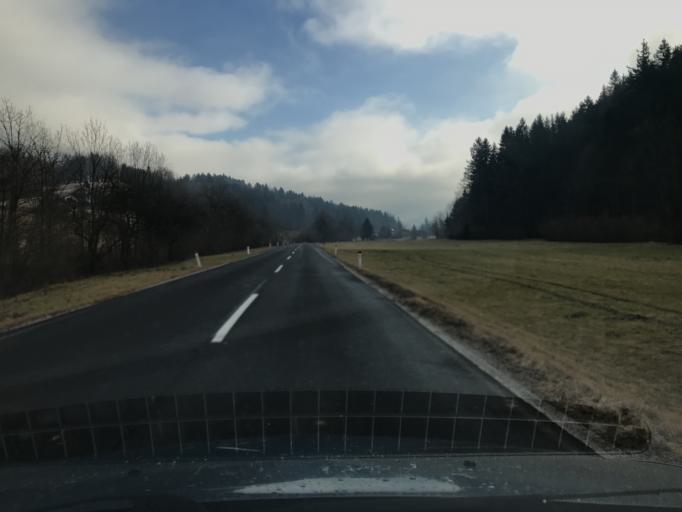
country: SI
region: Lukovica
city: Lukovica pri Domzalah
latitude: 46.2181
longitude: 14.7400
